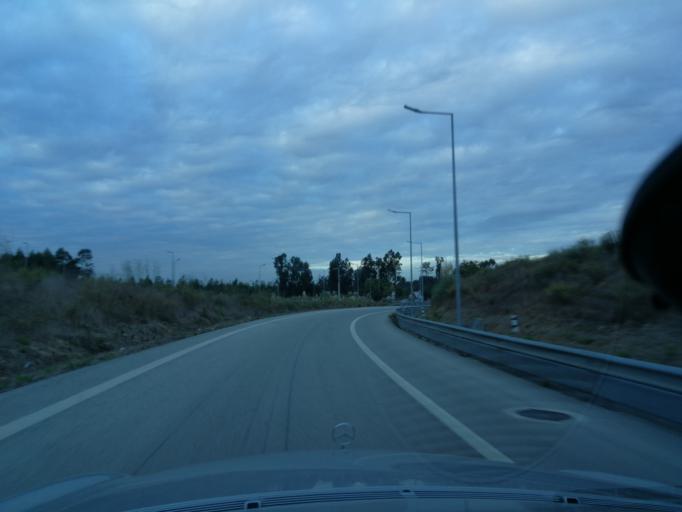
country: PT
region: Aveiro
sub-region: Estarreja
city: Salreu
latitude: 40.6890
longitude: -8.5430
